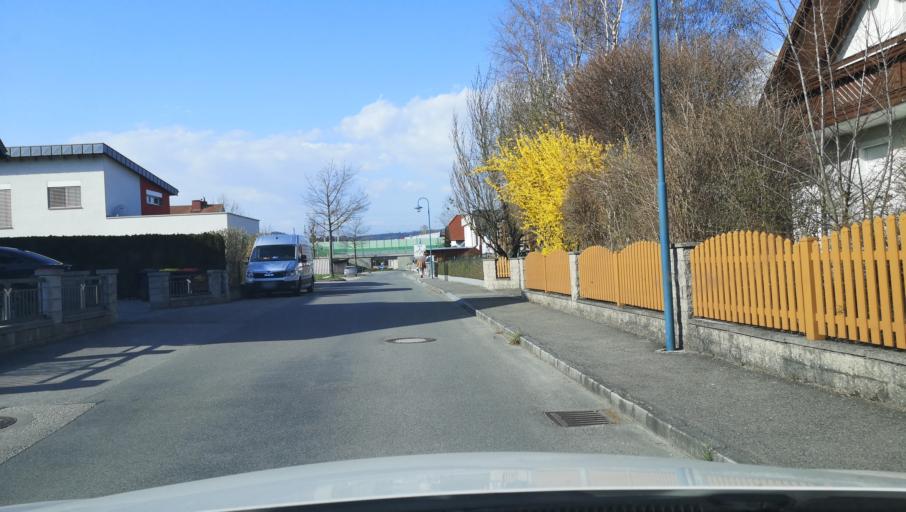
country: AT
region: Lower Austria
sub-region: Politischer Bezirk Melk
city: Blindenmarkt
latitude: 48.1235
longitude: 14.9878
